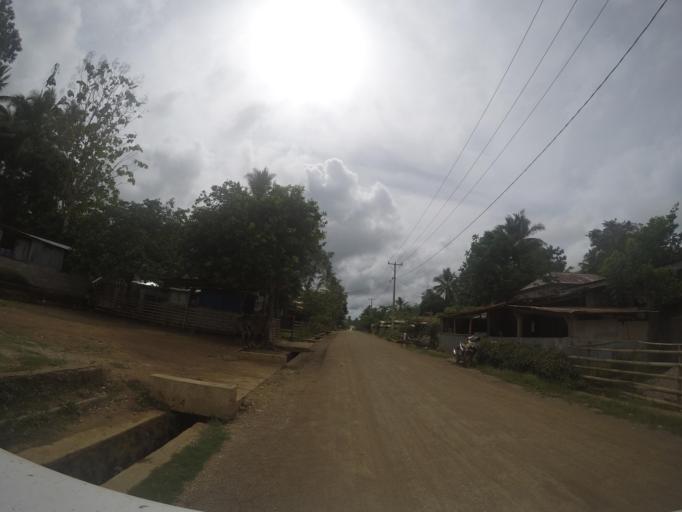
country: TL
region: Lautem
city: Lospalos
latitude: -8.5037
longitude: 126.9702
